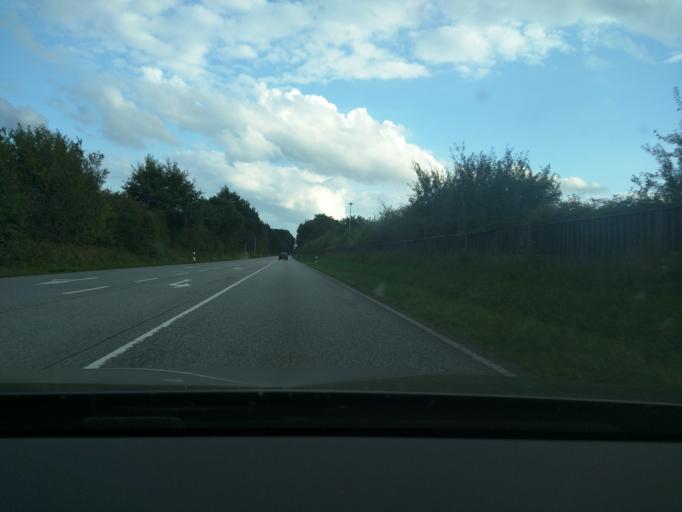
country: DE
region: Schleswig-Holstein
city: Kasseburg
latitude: 53.5547
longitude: 10.4133
